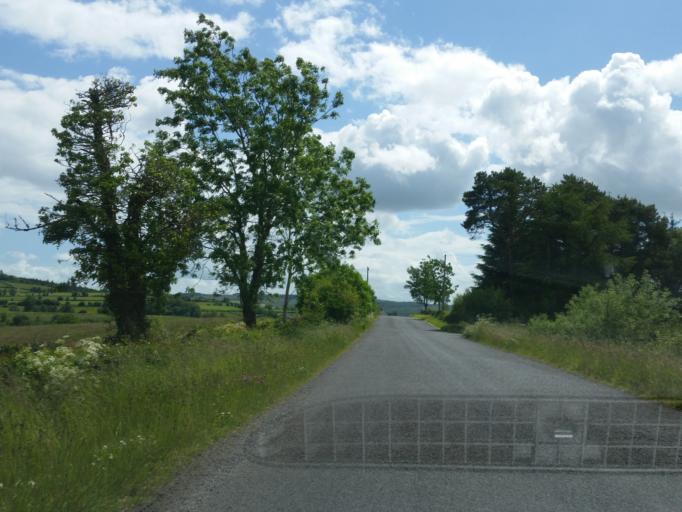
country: GB
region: Northern Ireland
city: Fivemiletown
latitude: 54.3512
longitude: -7.2977
